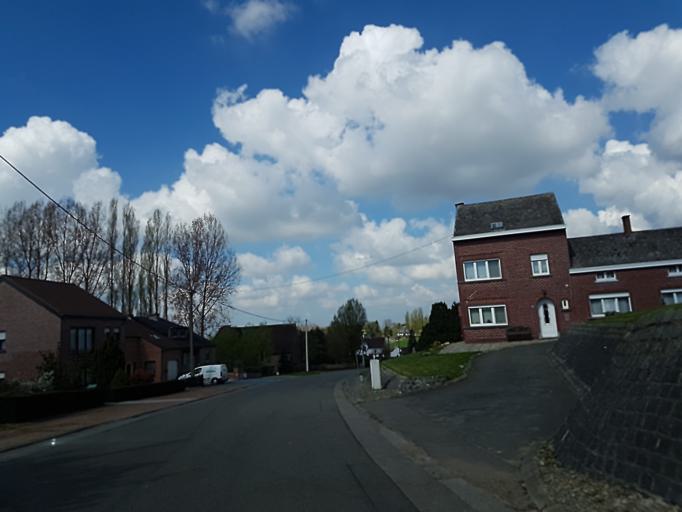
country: BE
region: Flanders
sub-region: Provincie Vlaams-Brabant
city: Gooik
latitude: 50.8195
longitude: 4.1195
